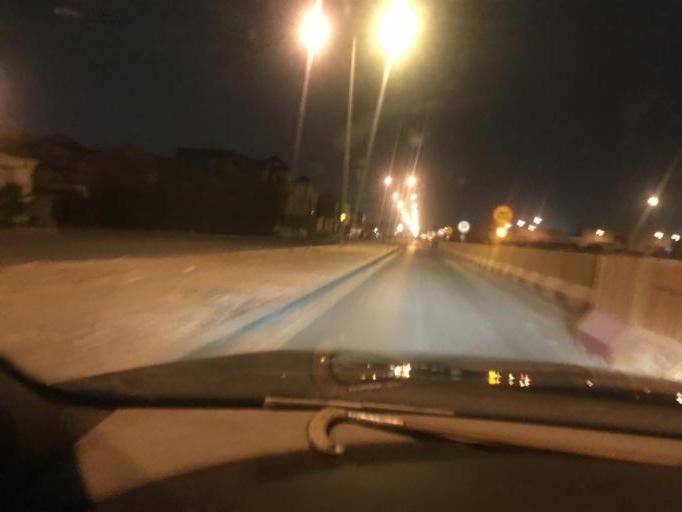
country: SA
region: Ar Riyad
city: Riyadh
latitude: 24.8049
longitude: 46.6782
